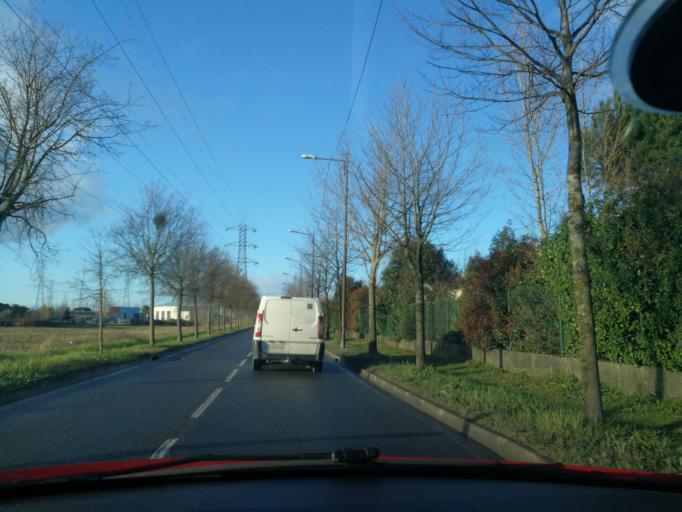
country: FR
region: Midi-Pyrenees
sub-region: Departement de la Haute-Garonne
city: Blagnac
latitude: 43.6329
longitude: 1.4171
